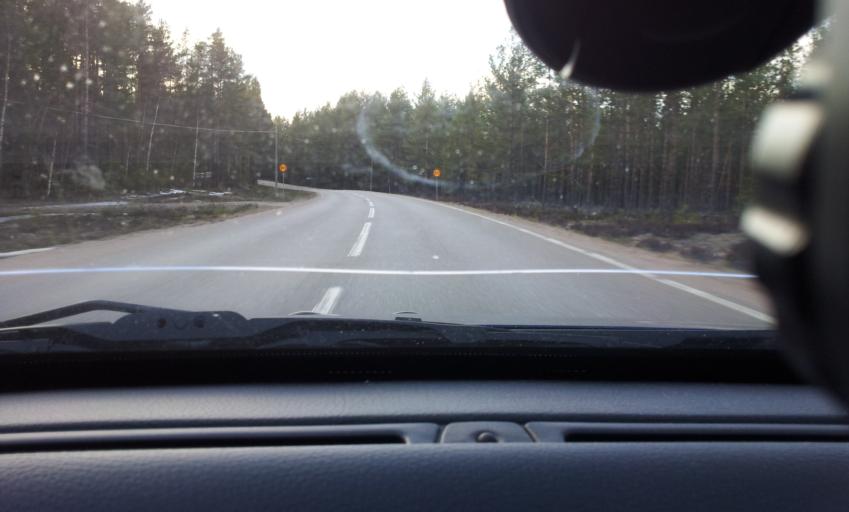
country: SE
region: Jaemtland
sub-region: Harjedalens Kommun
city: Sveg
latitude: 62.1237
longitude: 15.0342
